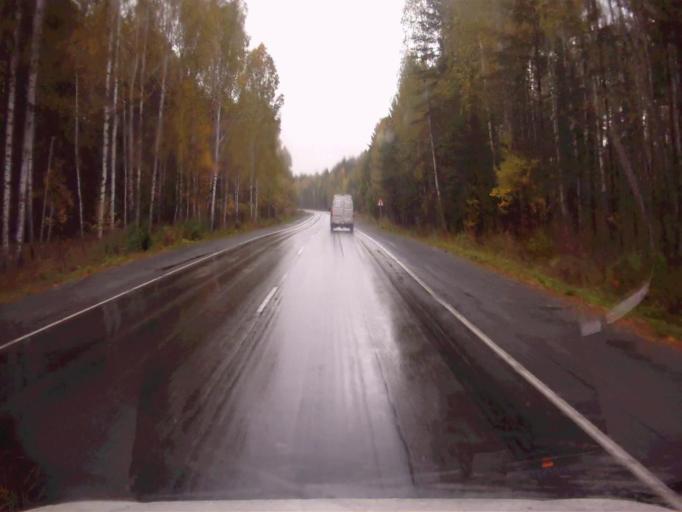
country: RU
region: Chelyabinsk
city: Tayginka
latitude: 55.5664
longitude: 60.6501
